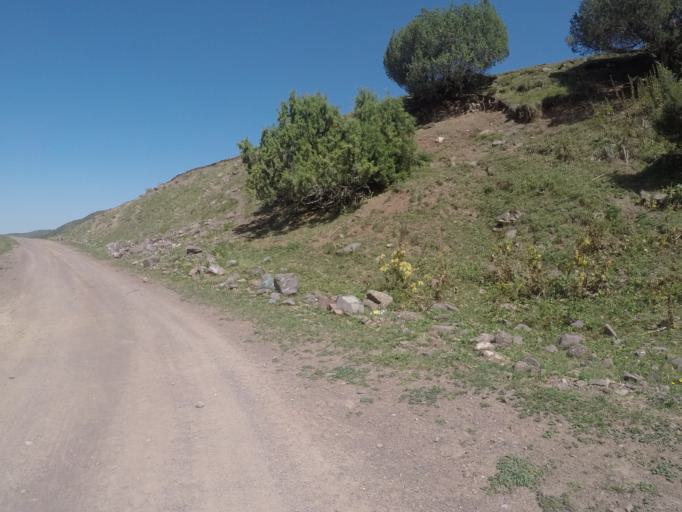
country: KG
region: Chuy
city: Bishkek
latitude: 42.6431
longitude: 74.5712
